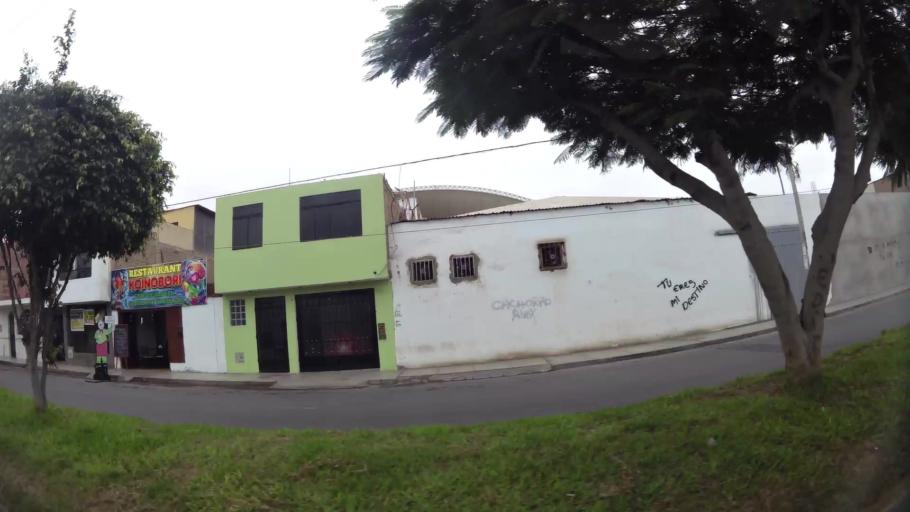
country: PE
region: Ica
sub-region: Provincia de Pisco
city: Pisco
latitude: -13.7091
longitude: -76.2079
